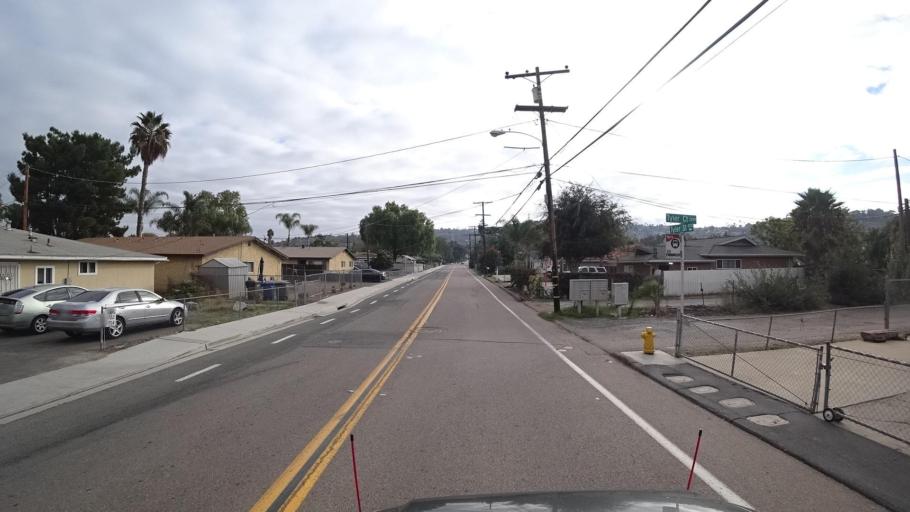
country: US
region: California
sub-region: San Diego County
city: Spring Valley
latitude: 32.7304
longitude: -117.0123
